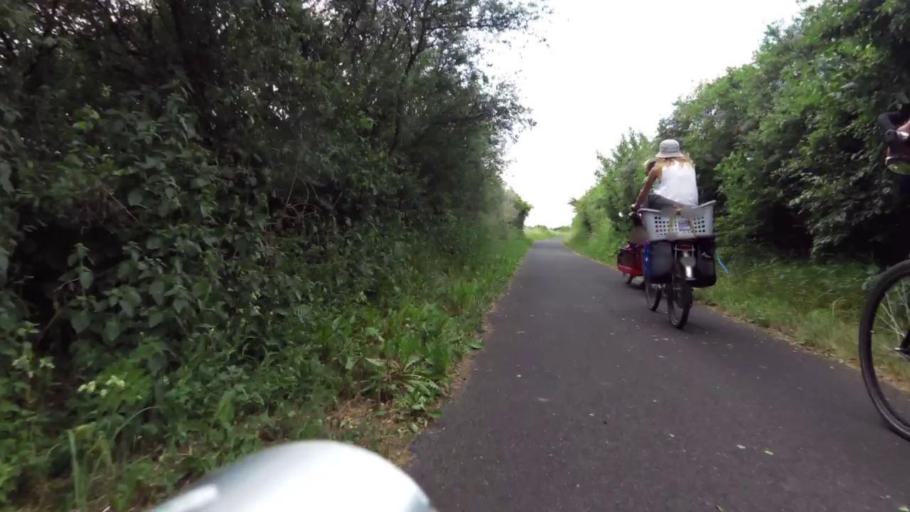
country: PL
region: Kujawsko-Pomorskie
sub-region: Powiat torunski
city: Lubianka
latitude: 53.1183
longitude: 18.4691
